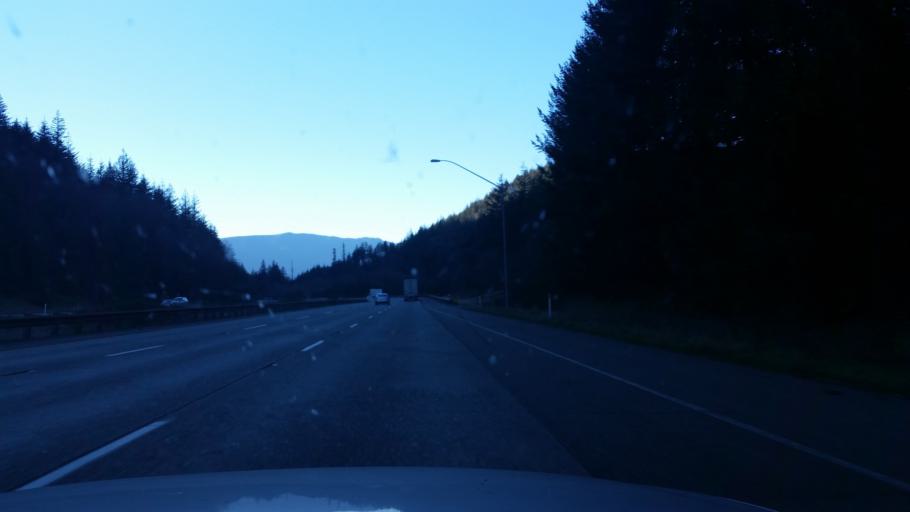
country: US
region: Washington
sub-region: King County
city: Tanner
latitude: 47.4436
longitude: -121.6750
